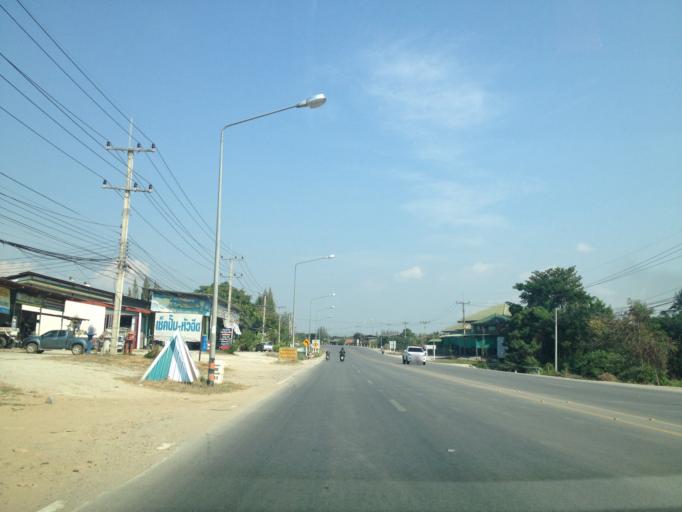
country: TH
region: Chiang Mai
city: Hot
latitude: 18.2042
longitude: 98.6154
